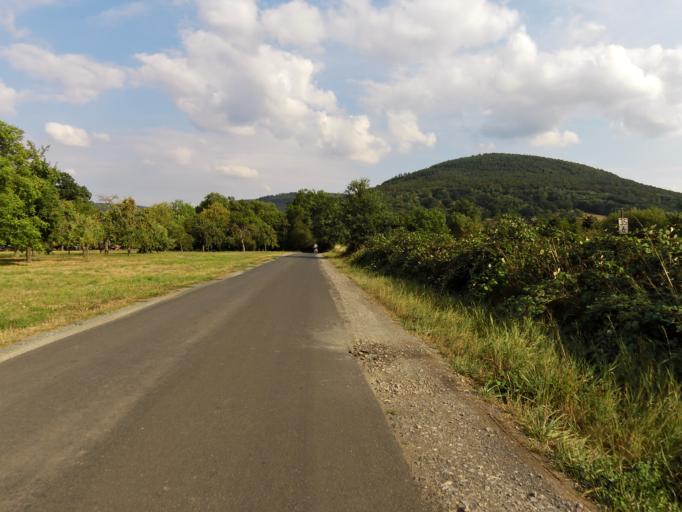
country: DE
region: Bavaria
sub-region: Regierungsbezirk Unterfranken
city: Kleinheubach
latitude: 49.7087
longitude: 9.2293
